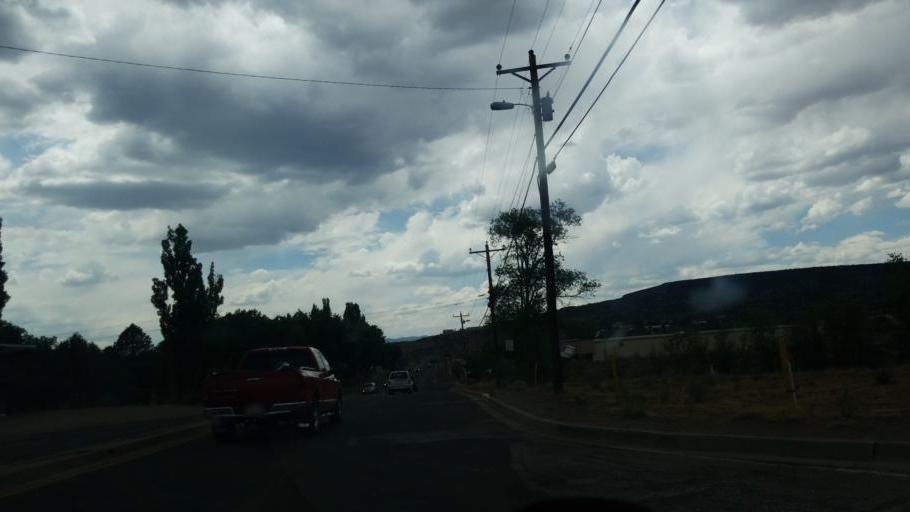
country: US
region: New Mexico
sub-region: Cibola County
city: Grants
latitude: 35.1613
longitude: -107.8344
